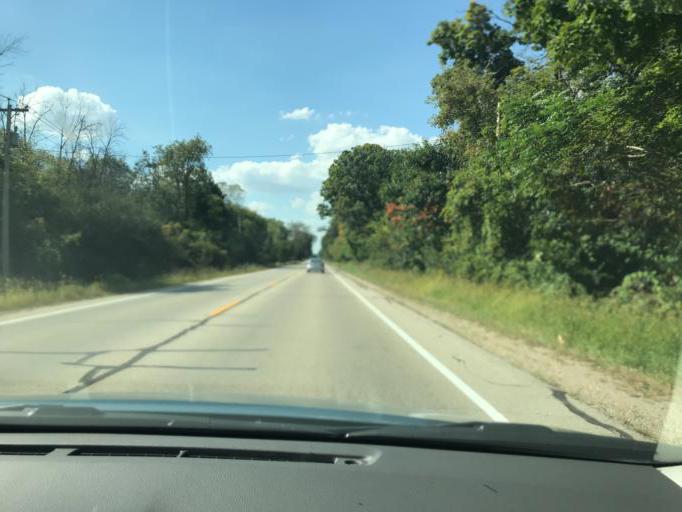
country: US
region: Wisconsin
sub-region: Walworth County
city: Williams Bay
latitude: 42.6036
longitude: -88.5483
